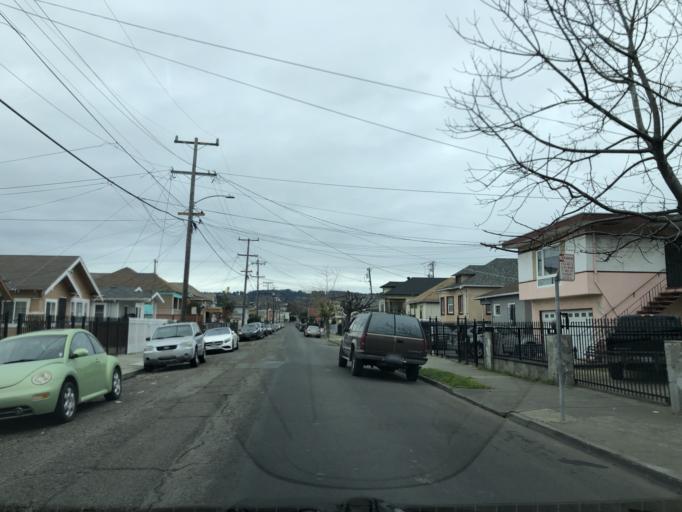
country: US
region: California
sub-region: Alameda County
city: San Leandro
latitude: 37.7438
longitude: -122.1738
